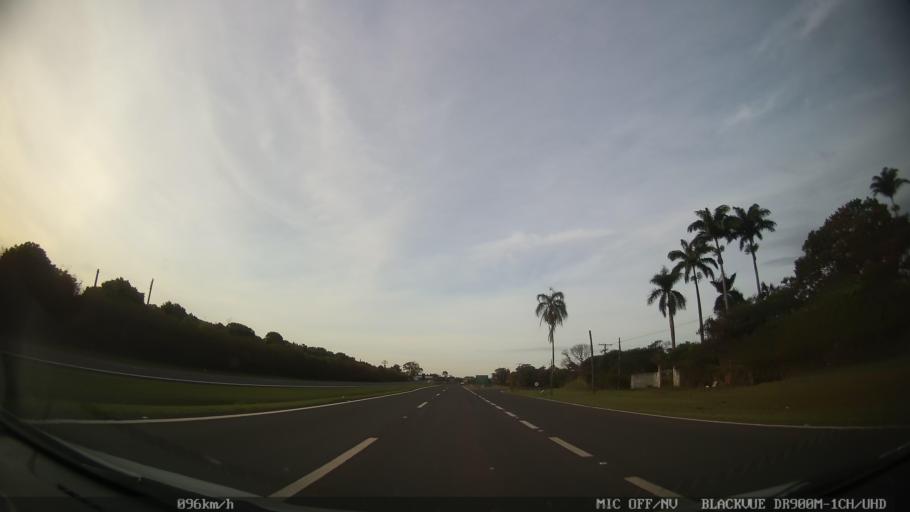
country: BR
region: Sao Paulo
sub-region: Iracemapolis
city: Iracemapolis
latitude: -22.6000
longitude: -47.4719
